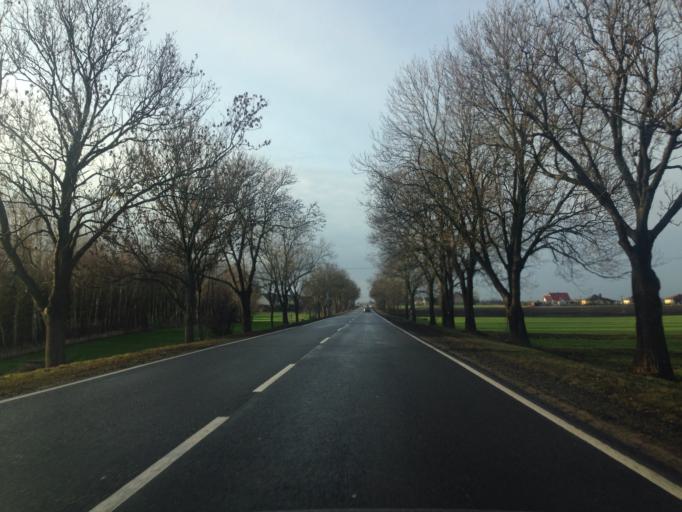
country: PL
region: Kujawsko-Pomorskie
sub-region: Powiat torunski
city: Lubicz Gorny
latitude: 53.1019
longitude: 18.7882
